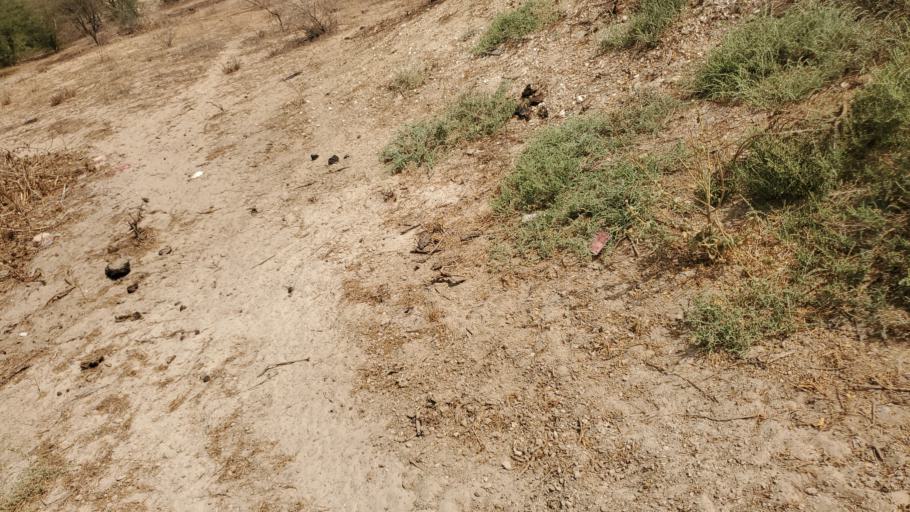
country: SN
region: Saint-Louis
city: Saint-Louis
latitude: 15.9506
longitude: -16.4311
